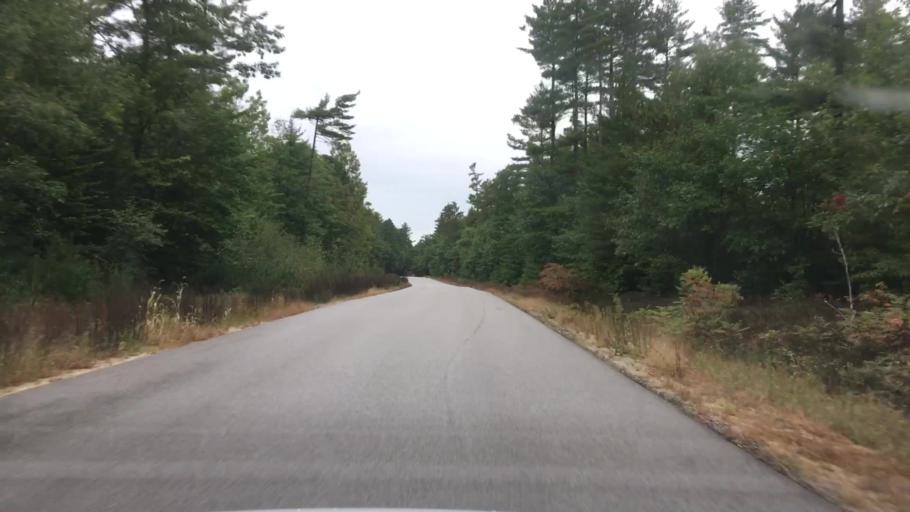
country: US
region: Maine
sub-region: Cumberland County
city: Harrison
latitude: 44.0280
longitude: -70.5940
